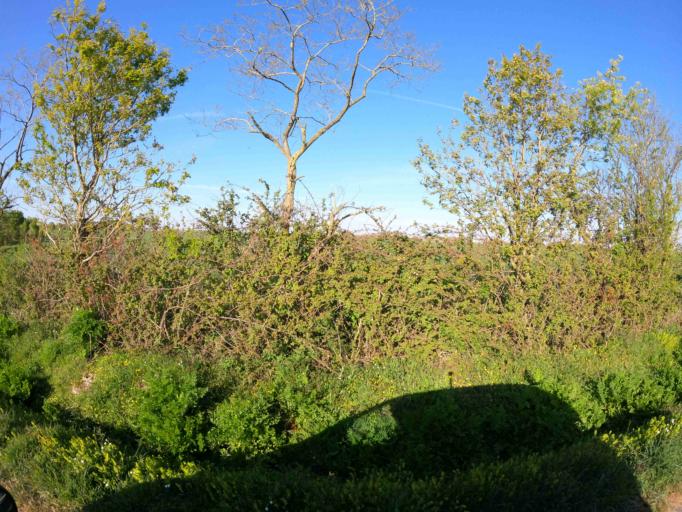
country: FR
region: Pays de la Loire
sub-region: Departement de la Vendee
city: Les Brouzils
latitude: 46.8855
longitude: -1.3360
